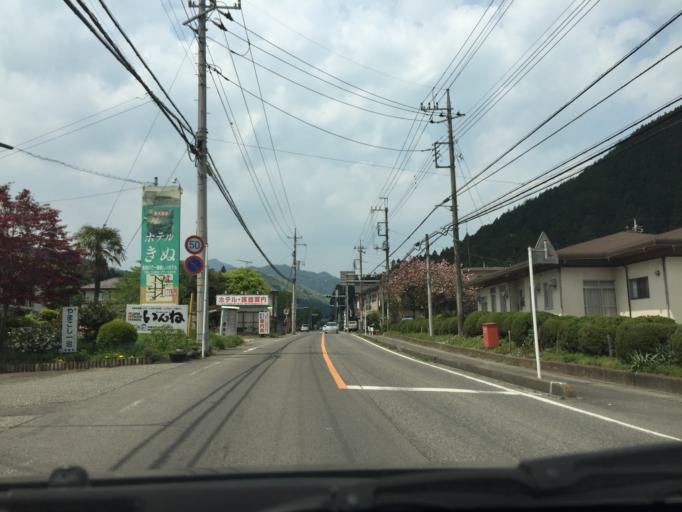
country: JP
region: Tochigi
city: Imaichi
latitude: 36.7869
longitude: 139.7072
